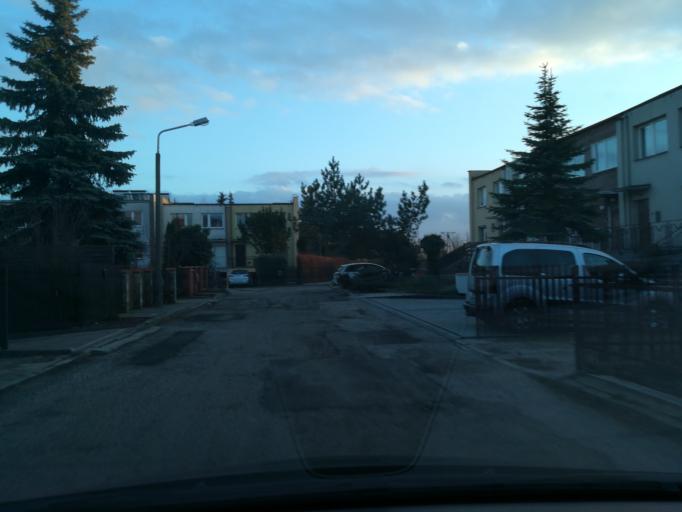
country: PL
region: Lodz Voivodeship
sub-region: Piotrkow Trybunalski
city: Piotrkow Trybunalski
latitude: 51.4073
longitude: 19.6582
